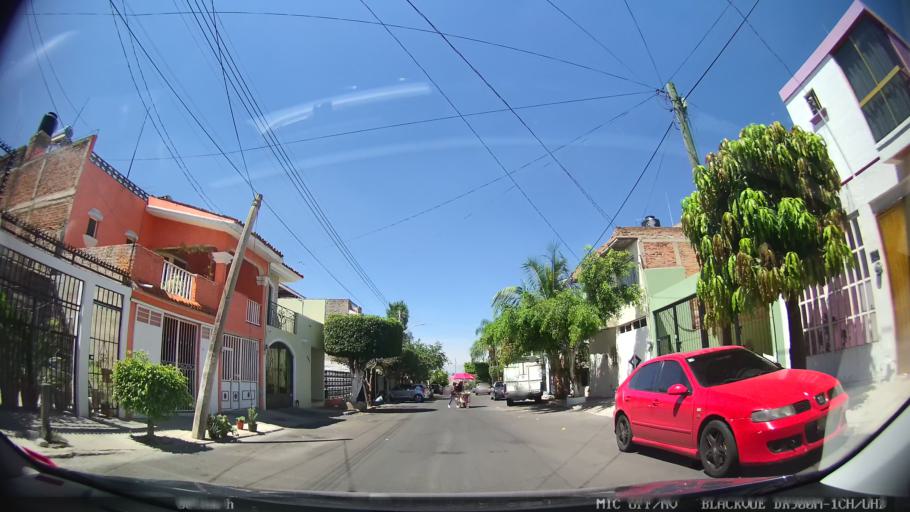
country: MX
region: Jalisco
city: Tlaquepaque
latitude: 20.6889
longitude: -103.2890
